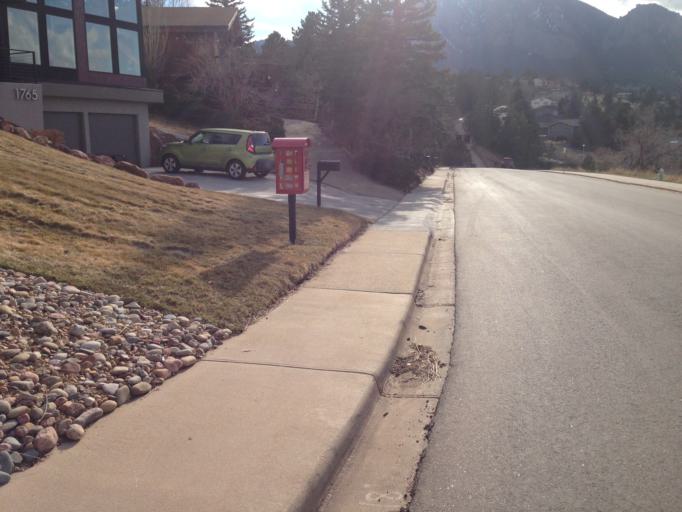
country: US
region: Colorado
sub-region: Boulder County
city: Boulder
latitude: 39.9704
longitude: -105.2479
